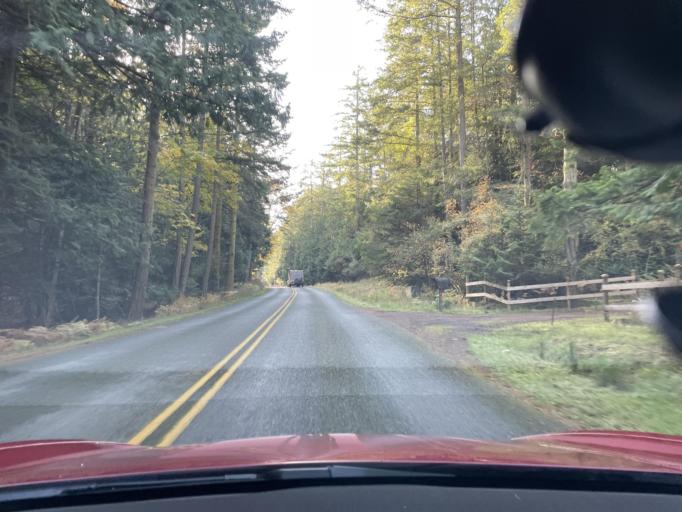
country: US
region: Washington
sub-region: San Juan County
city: Friday Harbor
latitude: 48.5328
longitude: -123.1586
